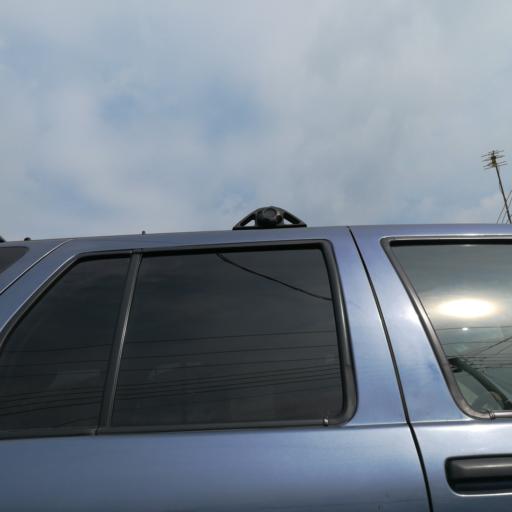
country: NG
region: Rivers
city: Port Harcourt
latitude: 4.8413
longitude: 7.0701
